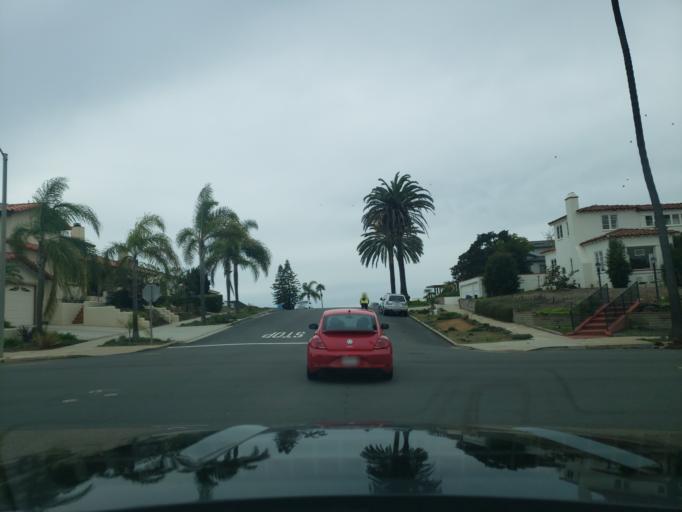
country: US
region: California
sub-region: San Diego County
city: Coronado
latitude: 32.7354
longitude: -117.2449
